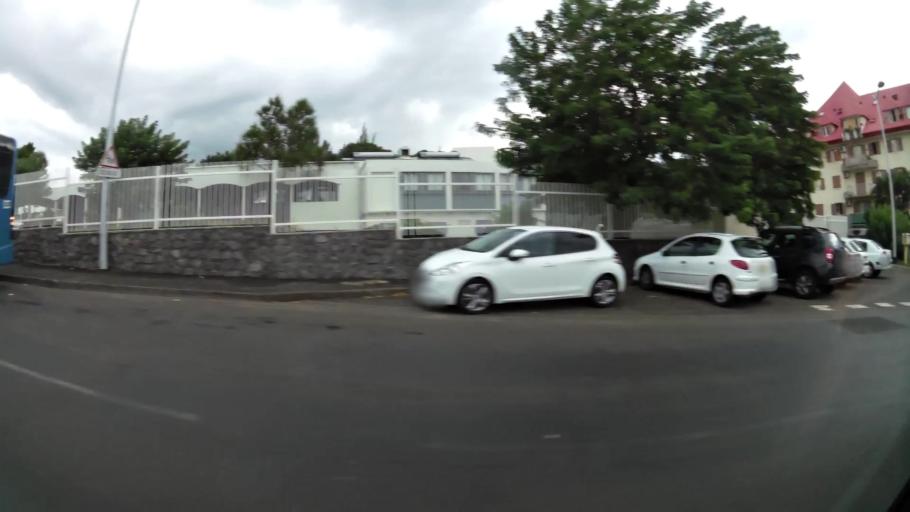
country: RE
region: Reunion
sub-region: Reunion
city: Saint-Denis
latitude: -20.9015
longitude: 55.4682
